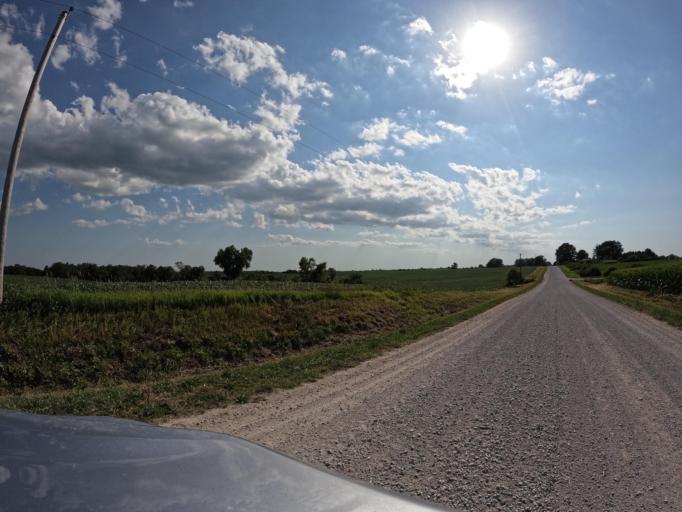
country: US
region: Iowa
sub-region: Appanoose County
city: Centerville
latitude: 40.7178
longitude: -93.0149
